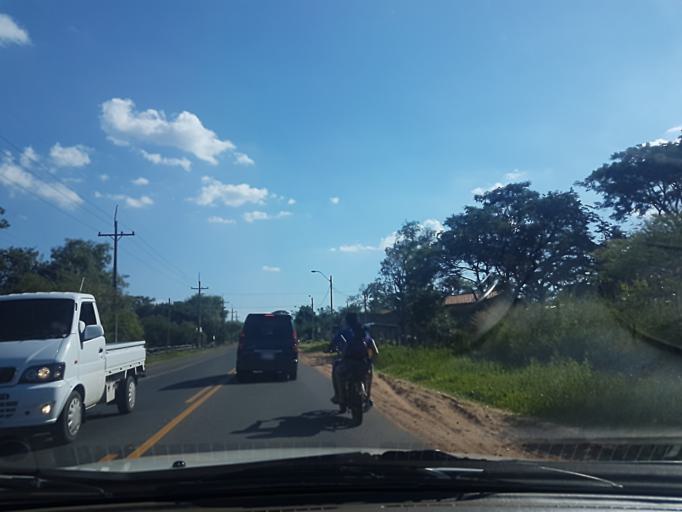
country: PY
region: Central
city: Aregua
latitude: -25.2314
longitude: -57.4189
